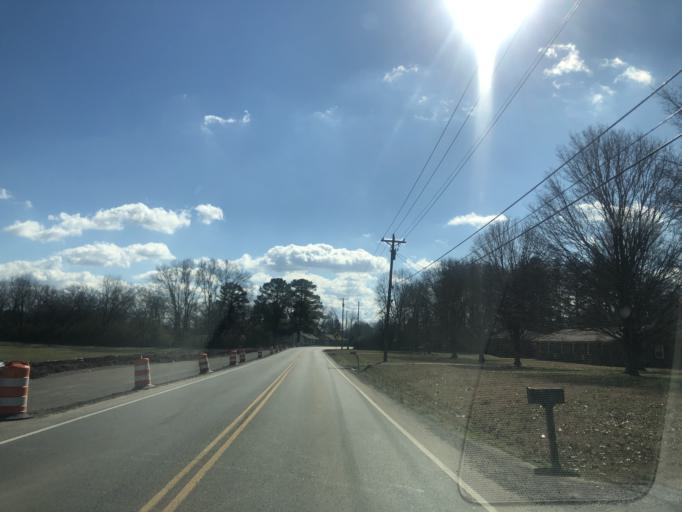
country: US
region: Tennessee
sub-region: Rutherford County
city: Smyrna
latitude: 35.8803
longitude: -86.4967
